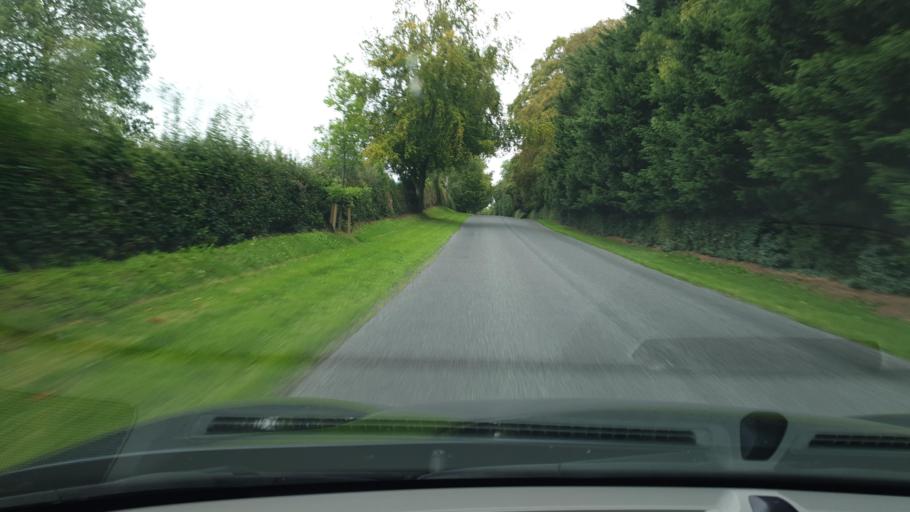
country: IE
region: Leinster
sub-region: Kildare
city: Maynooth
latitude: 53.3996
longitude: -6.6180
